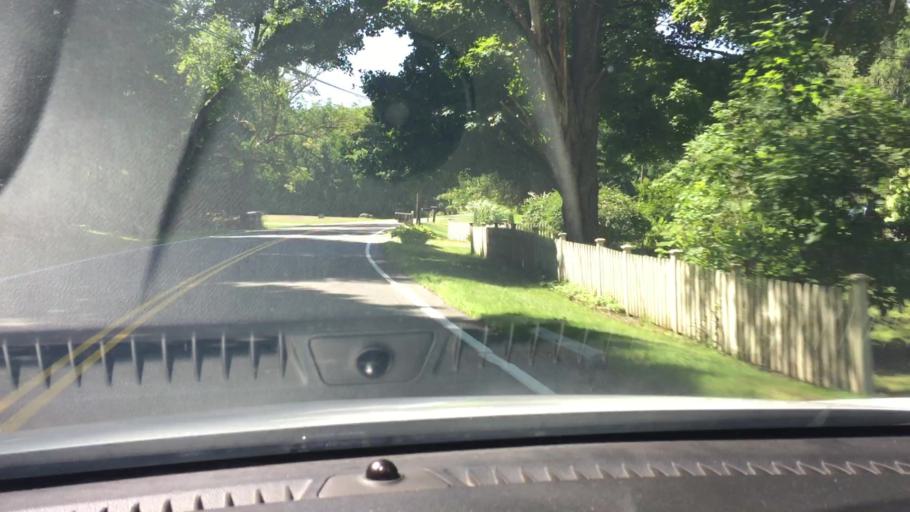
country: US
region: Massachusetts
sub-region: Berkshire County
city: Lenox
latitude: 42.3805
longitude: -73.2566
